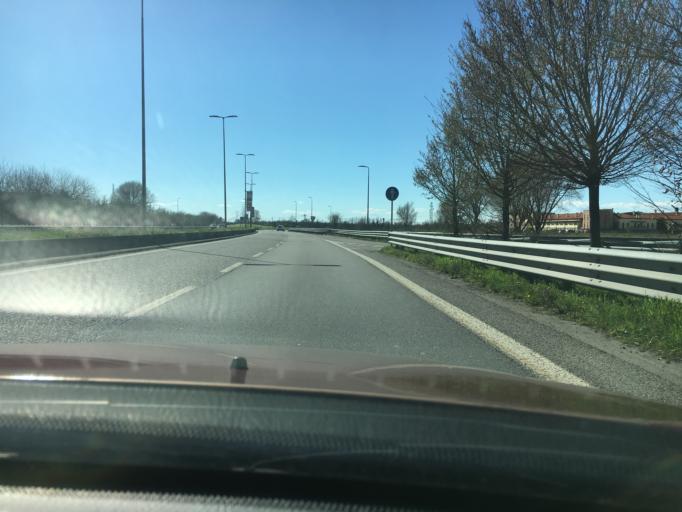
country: IT
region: Lombardy
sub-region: Citta metropolitana di Milano
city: Settimo Milanese
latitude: 45.4571
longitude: 9.0659
